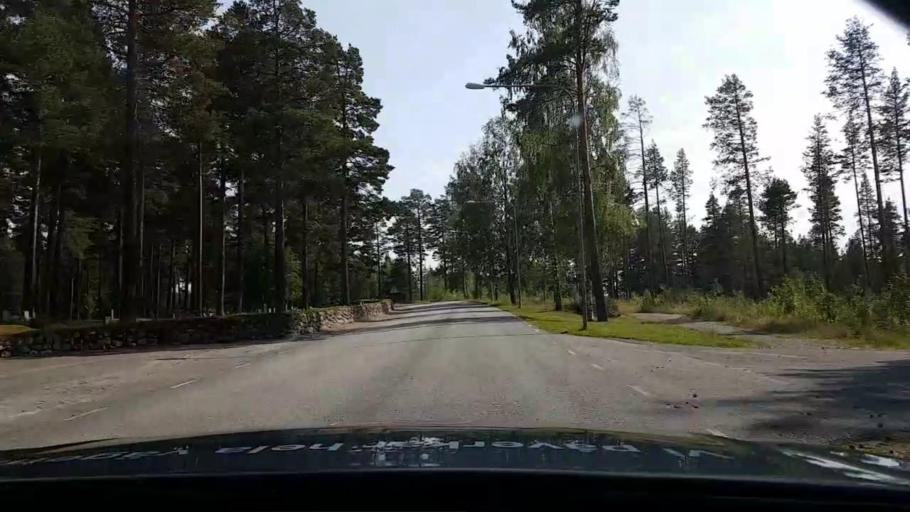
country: SE
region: Jaemtland
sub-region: Braecke Kommun
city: Braecke
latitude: 62.7427
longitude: 15.4319
